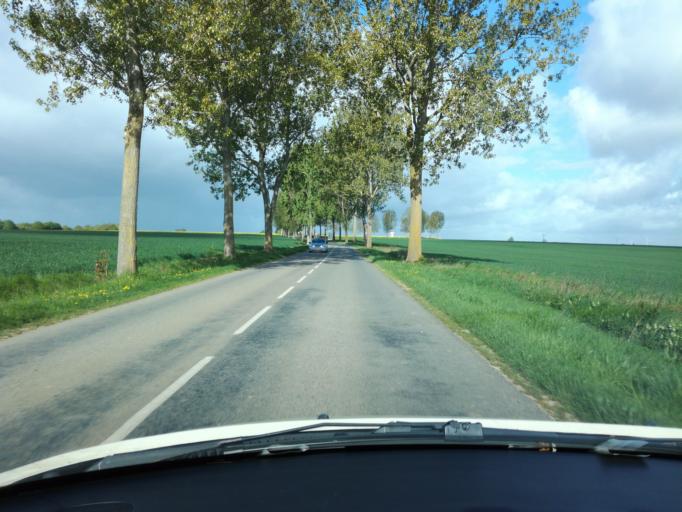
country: FR
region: Picardie
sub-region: Departement de la Somme
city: Hornoy-le-Bourg
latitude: 49.8538
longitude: 1.8655
